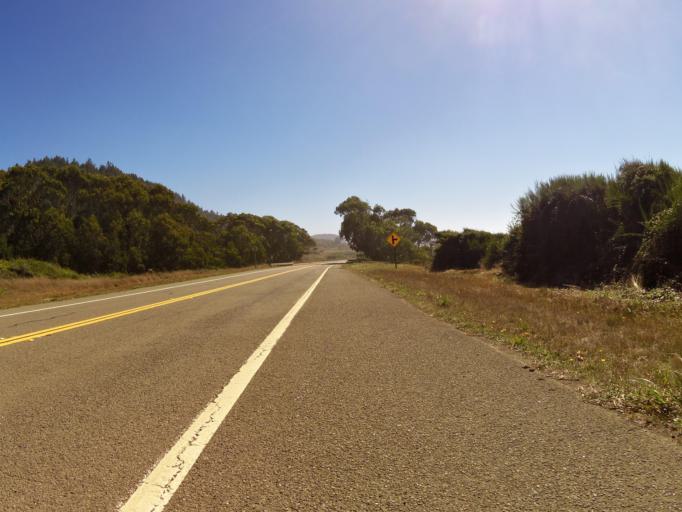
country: US
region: California
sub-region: Mendocino County
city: Fort Bragg
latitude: 39.6795
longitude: -123.7903
